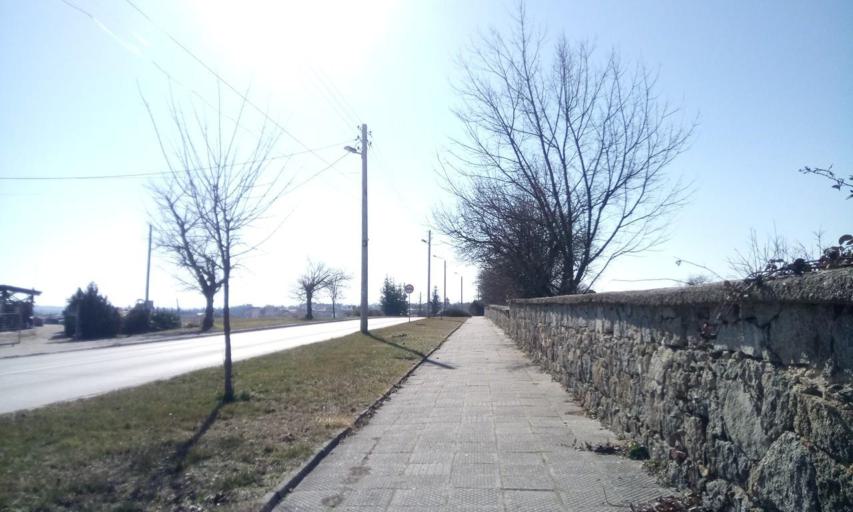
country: BG
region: Plovdiv
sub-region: Obshtina Khisarya
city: Khisarya
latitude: 42.5144
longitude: 24.7178
